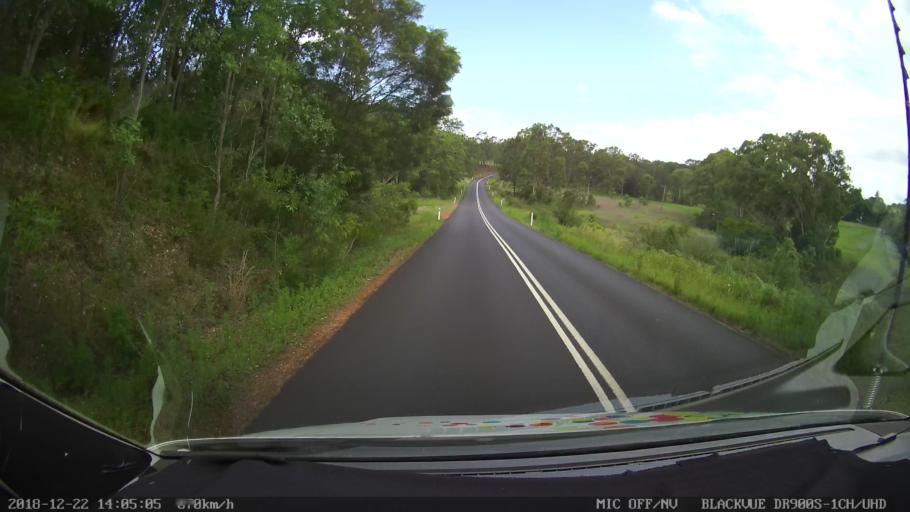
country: AU
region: New South Wales
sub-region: Clarence Valley
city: Coutts Crossing
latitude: -29.9411
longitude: 152.7274
